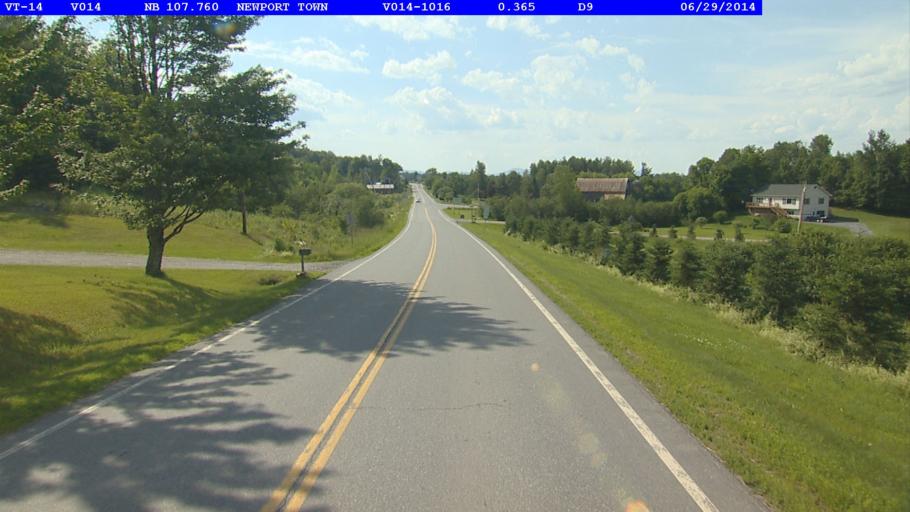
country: US
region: Vermont
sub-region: Orleans County
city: Newport
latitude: 44.9168
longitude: -72.2872
